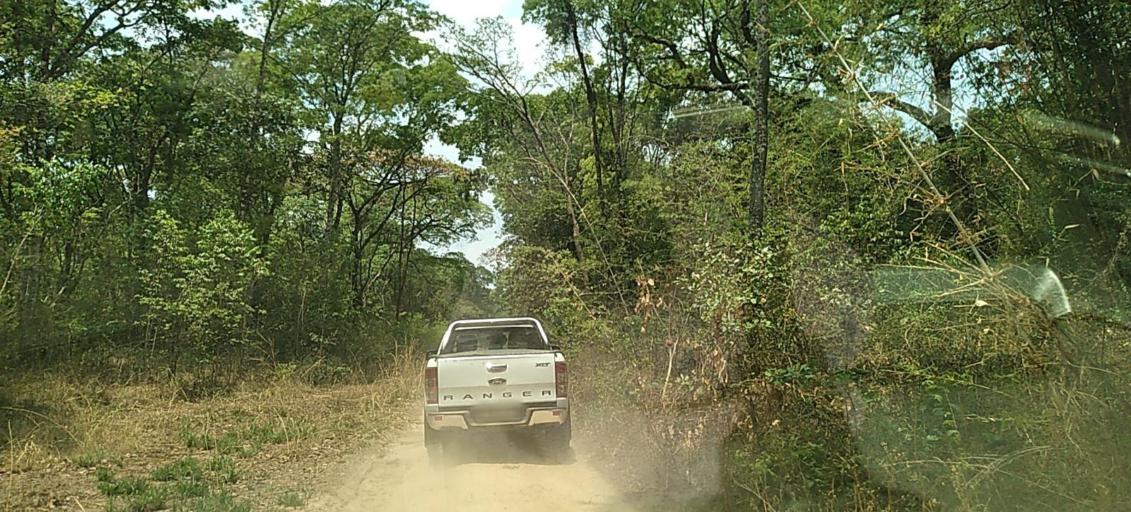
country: ZM
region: Copperbelt
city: Chingola
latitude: -12.7908
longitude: 27.6470
